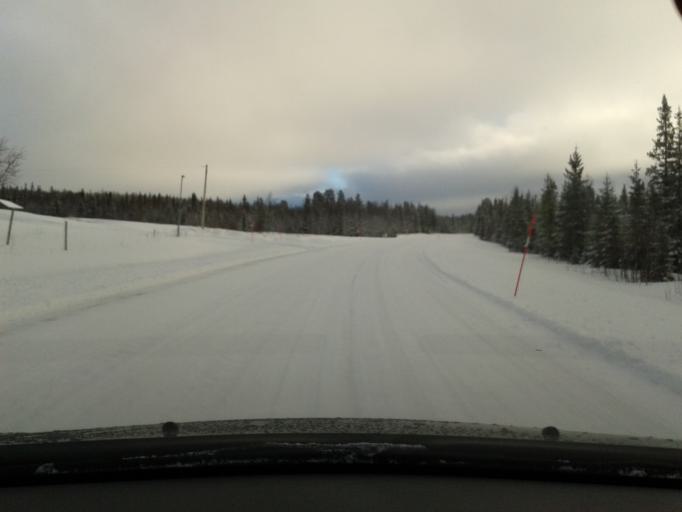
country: SE
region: Vaesterbotten
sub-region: Vilhelmina Kommun
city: Sjoberg
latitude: 65.2518
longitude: 15.6118
